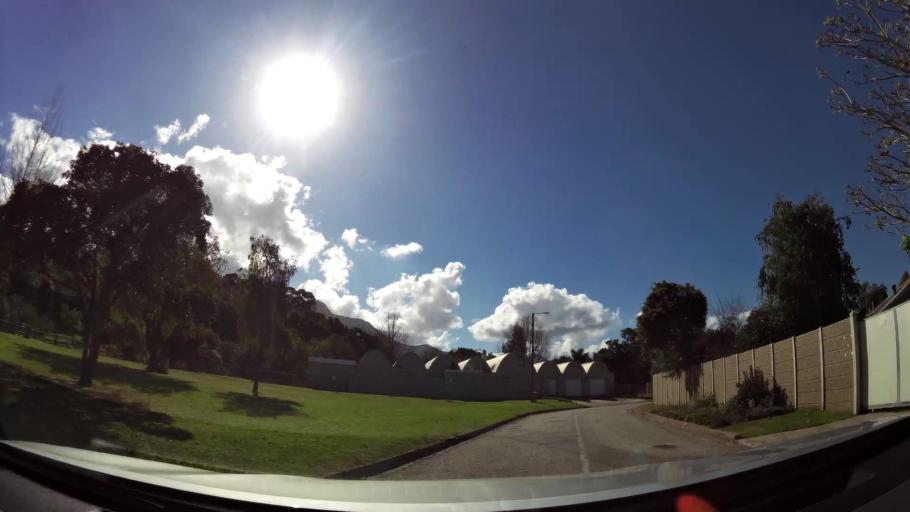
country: ZA
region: Western Cape
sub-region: Eden District Municipality
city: George
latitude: -33.9483
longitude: 22.4576
